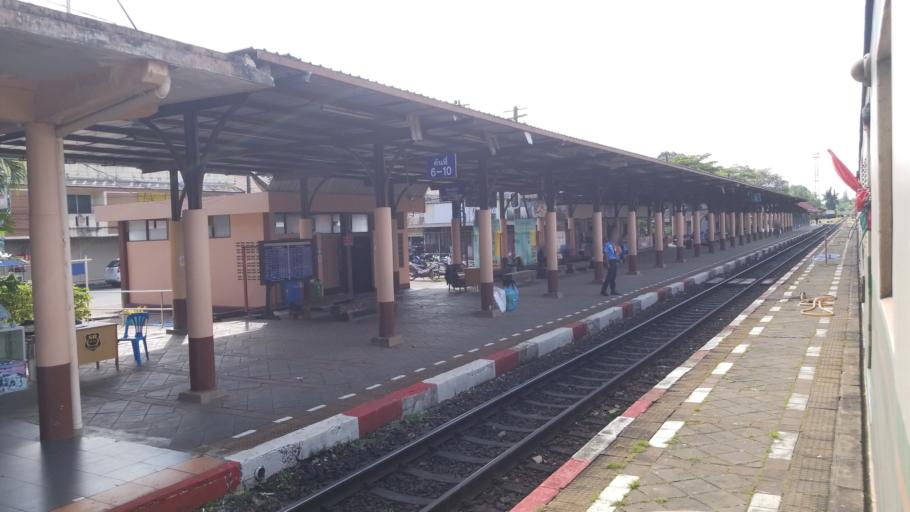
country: TH
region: Nakhon Si Thammarat
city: Thung Song
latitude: 8.1709
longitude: 99.6794
